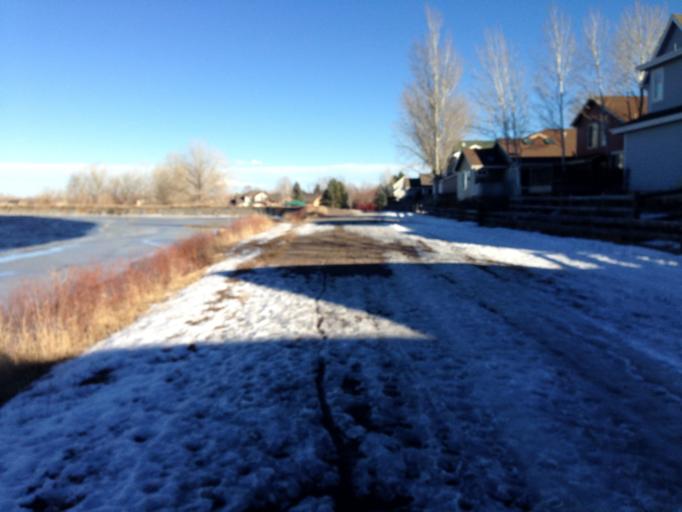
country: US
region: Colorado
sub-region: Boulder County
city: Lafayette
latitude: 40.0174
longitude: -105.0990
